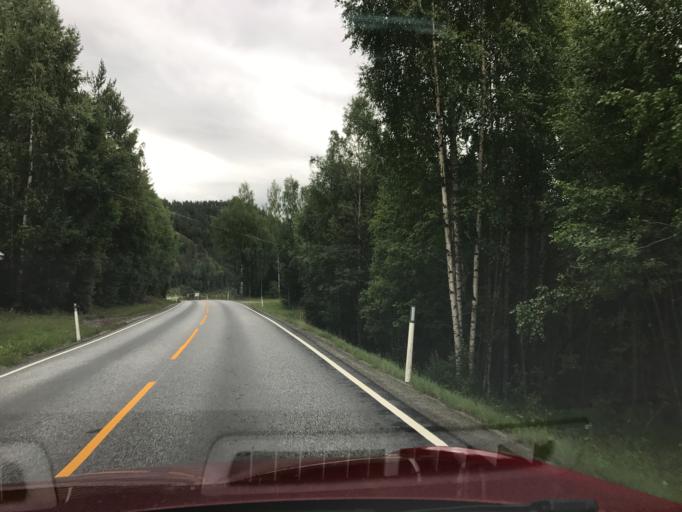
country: NO
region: Buskerud
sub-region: Nore og Uvdal
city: Rodberg
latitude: 60.2610
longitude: 8.8873
